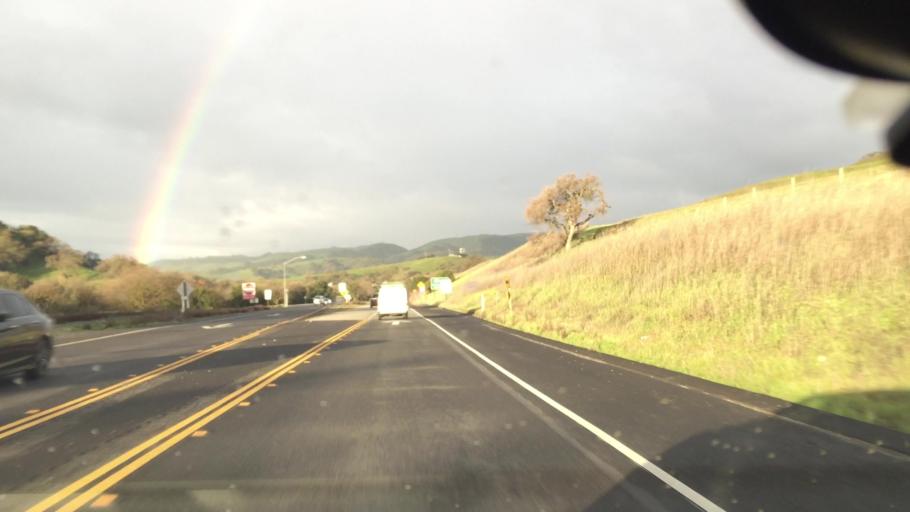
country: US
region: California
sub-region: Alameda County
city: Pleasanton
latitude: 37.5967
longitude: -121.8617
